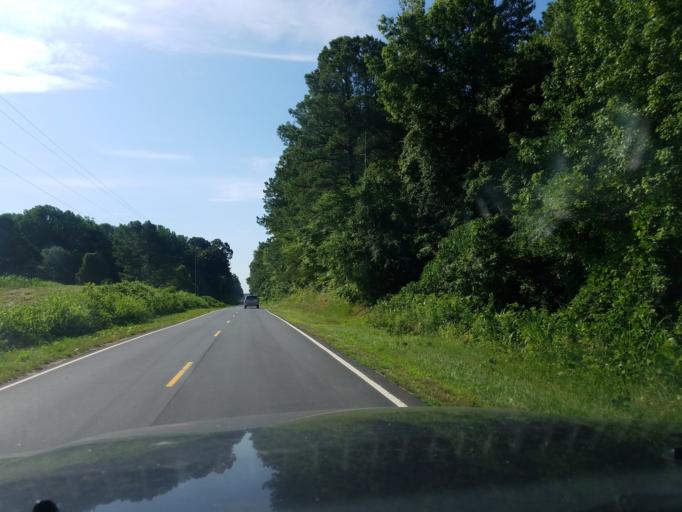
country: US
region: North Carolina
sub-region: Granville County
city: Butner
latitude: 36.1661
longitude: -78.7847
